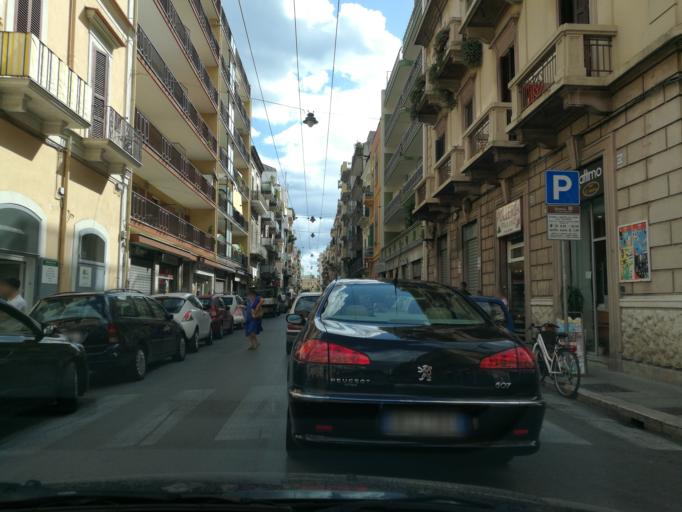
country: IT
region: Apulia
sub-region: Provincia di Bari
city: Bari
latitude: 41.1269
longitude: 16.8594
